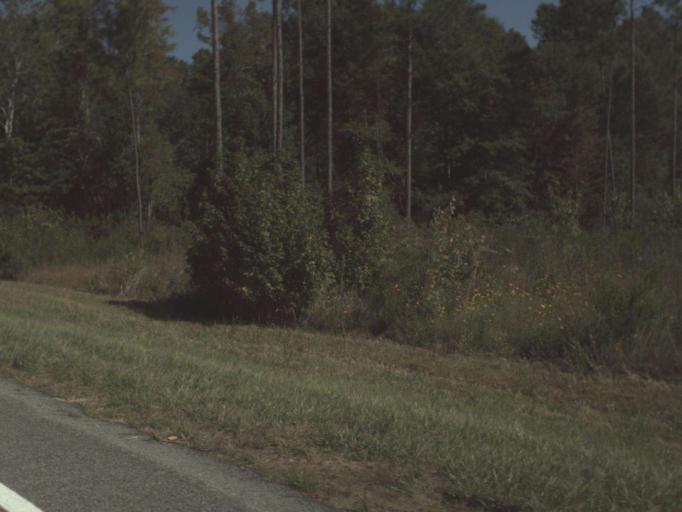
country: US
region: Florida
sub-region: Leon County
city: Woodville
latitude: 30.2571
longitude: -84.0425
